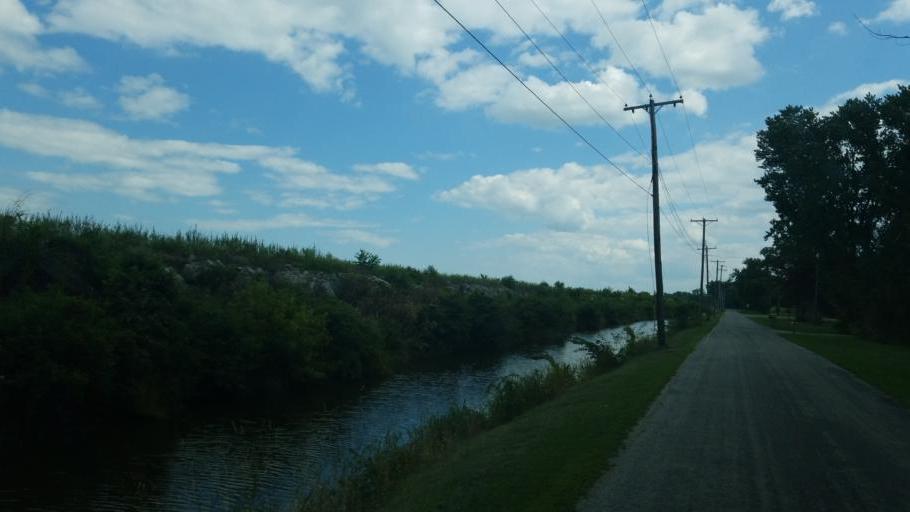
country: US
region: Ohio
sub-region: Lucas County
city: Curtice
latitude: 41.6700
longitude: -83.2750
